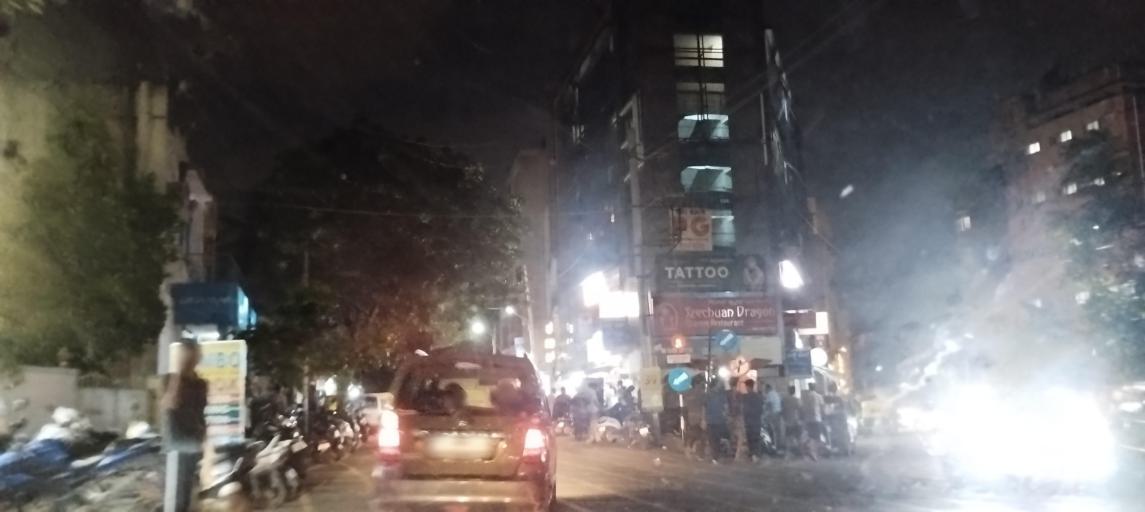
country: IN
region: Karnataka
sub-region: Bangalore Urban
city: Bangalore
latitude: 12.9398
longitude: 77.5643
